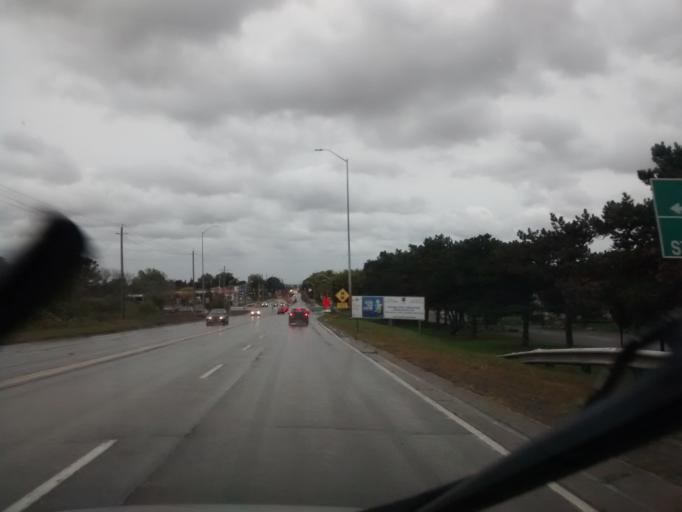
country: CA
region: Ontario
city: Hamilton
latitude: 43.2170
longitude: -79.7686
